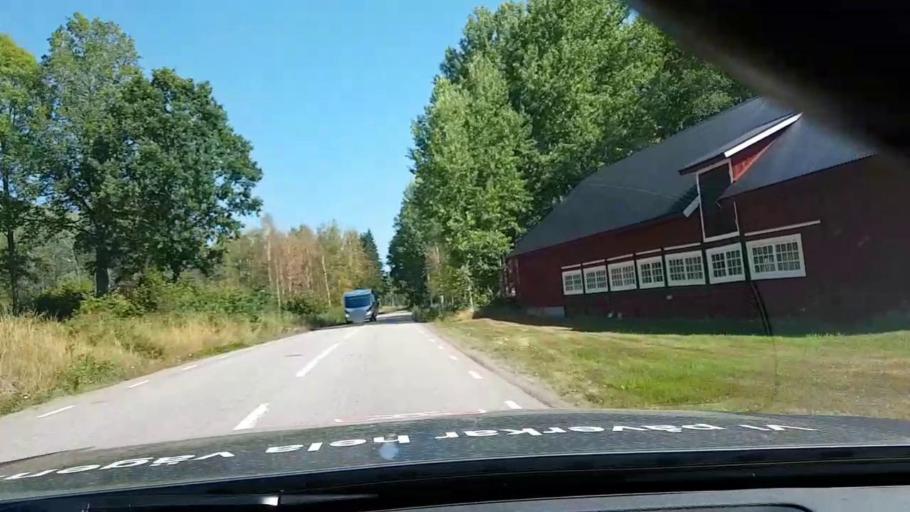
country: SE
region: Kalmar
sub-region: Hultsfreds Kommun
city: Virserum
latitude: 57.1307
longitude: 15.6571
